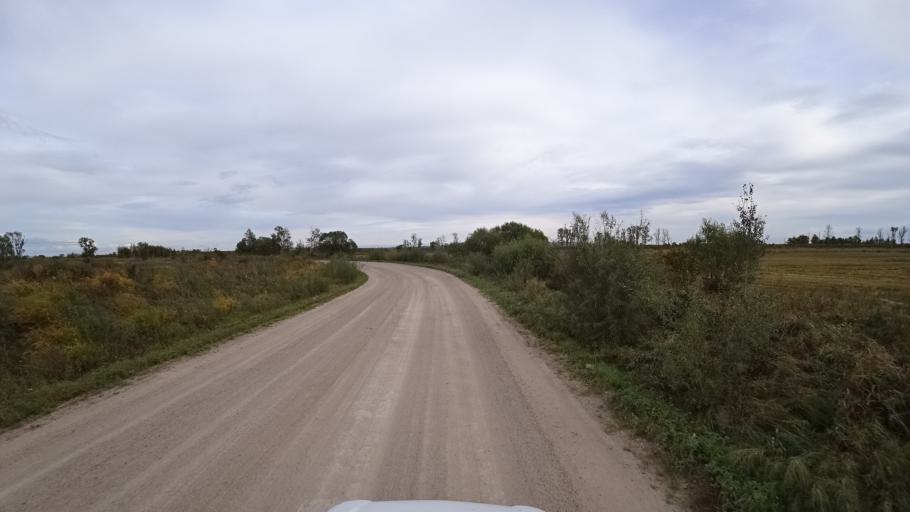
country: RU
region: Amur
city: Arkhara
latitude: 49.3746
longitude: 130.1570
